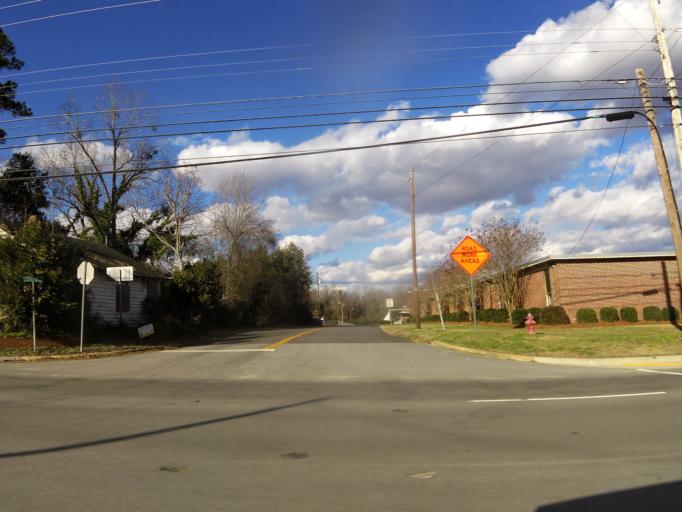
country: US
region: South Carolina
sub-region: Clarendon County
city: Manning
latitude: 33.6962
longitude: -80.2202
